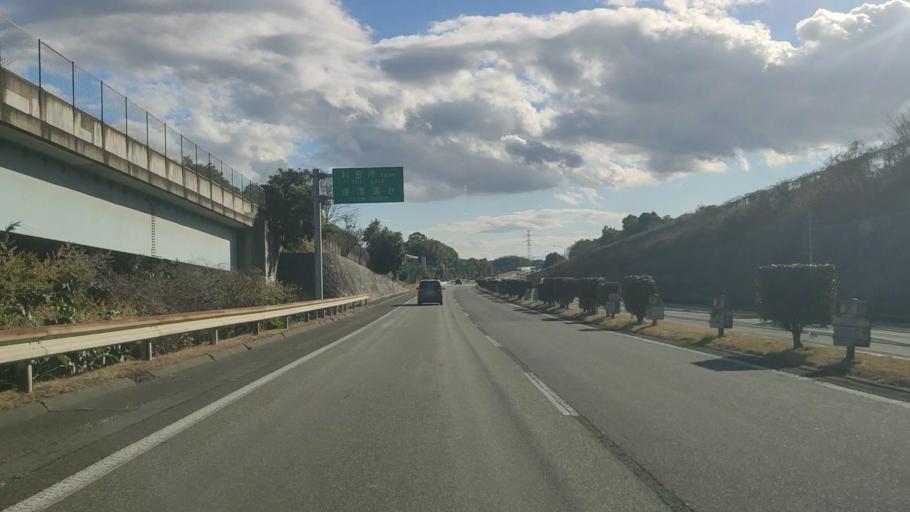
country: JP
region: Fukuoka
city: Nakama
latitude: 33.7907
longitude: 130.7453
